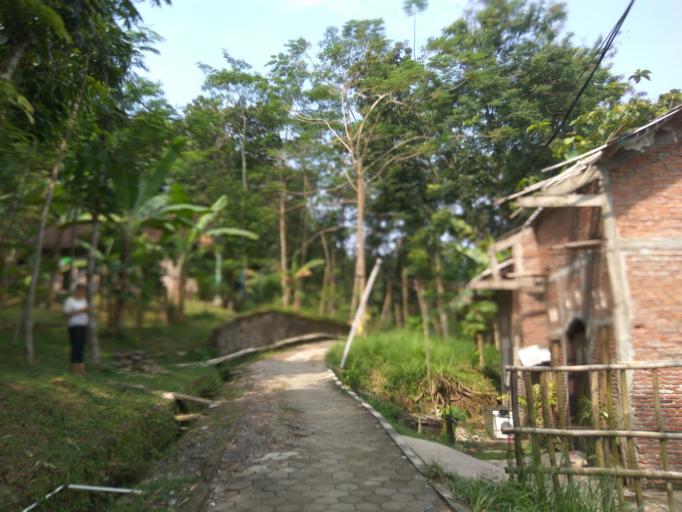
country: ID
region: Central Java
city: Semarang
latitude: -7.0361
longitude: 110.4081
